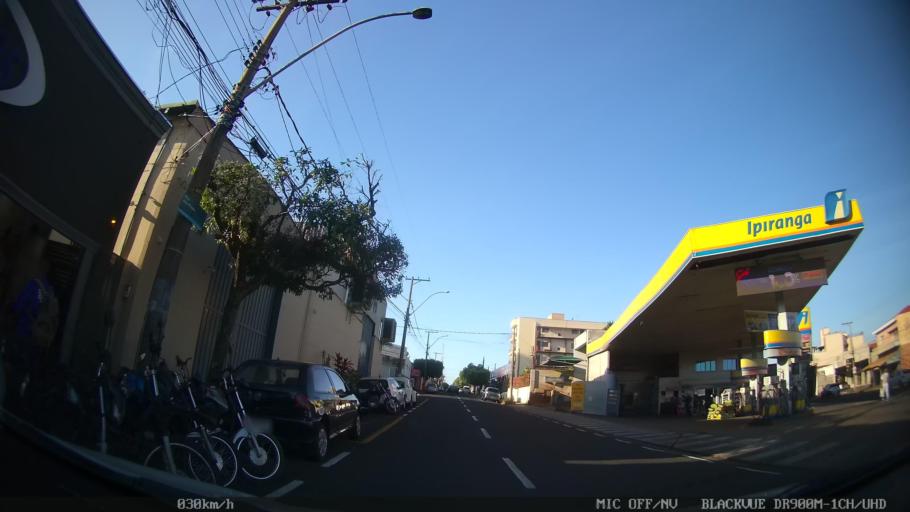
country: BR
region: Sao Paulo
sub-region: Sao Jose Do Rio Preto
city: Sao Jose do Rio Preto
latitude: -20.8050
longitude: -49.3716
